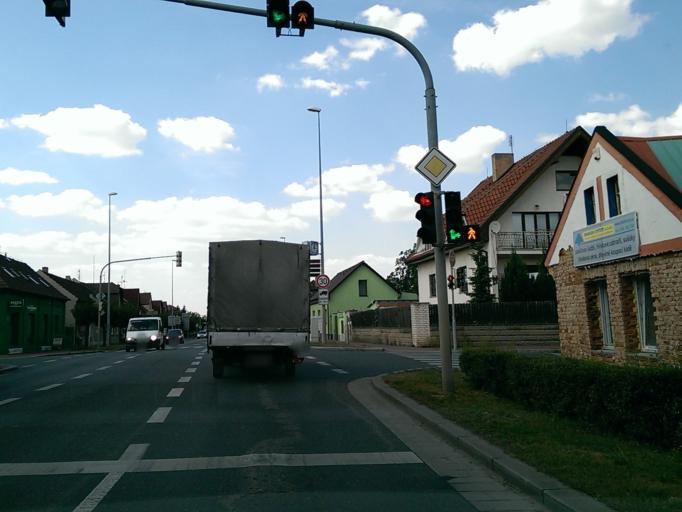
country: CZ
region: Praha
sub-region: Praha 14
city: Dolni Pocernice
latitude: 50.0589
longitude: 14.5596
